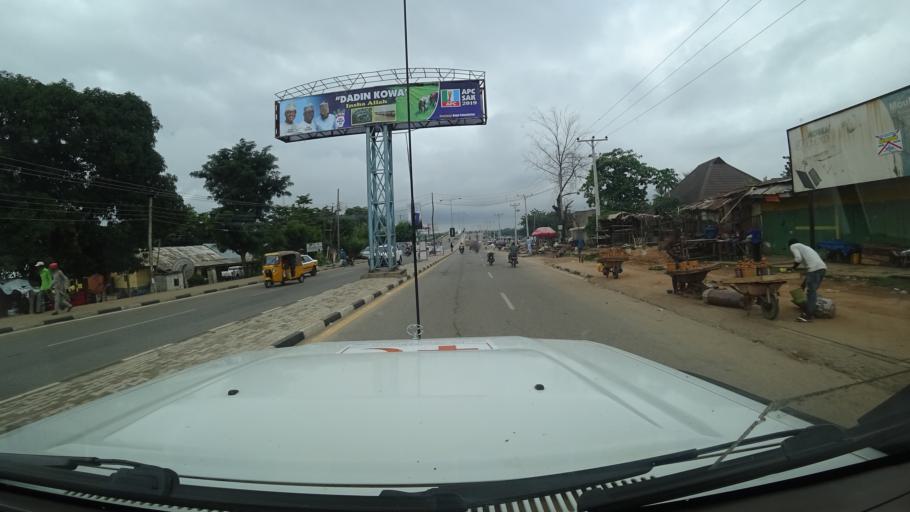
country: NG
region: Niger
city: Minna
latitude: 9.6112
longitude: 6.5508
